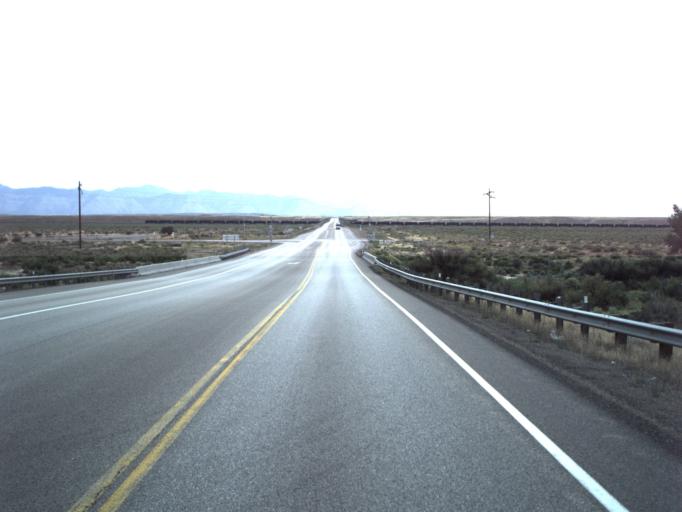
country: US
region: Utah
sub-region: Carbon County
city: Wellington
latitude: 39.5270
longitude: -110.5763
